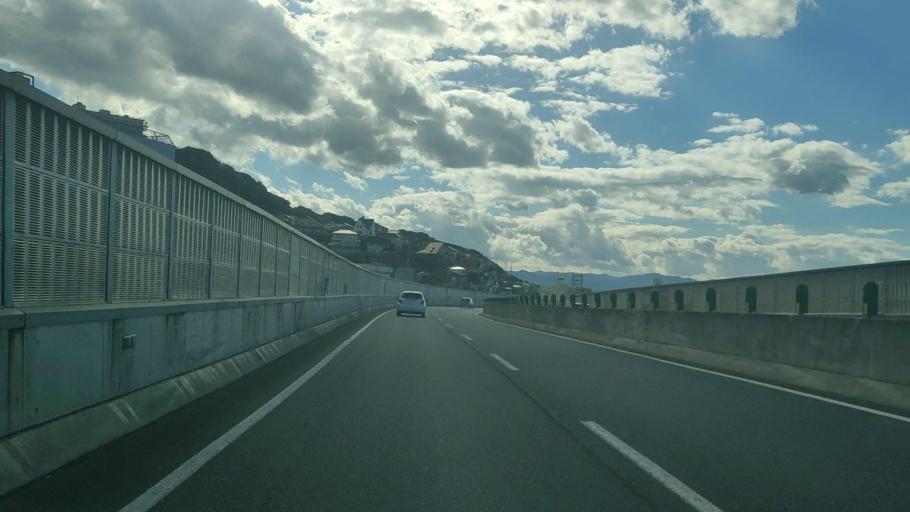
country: JP
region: Yamaguchi
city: Shimonoseki
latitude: 33.8831
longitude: 130.9060
